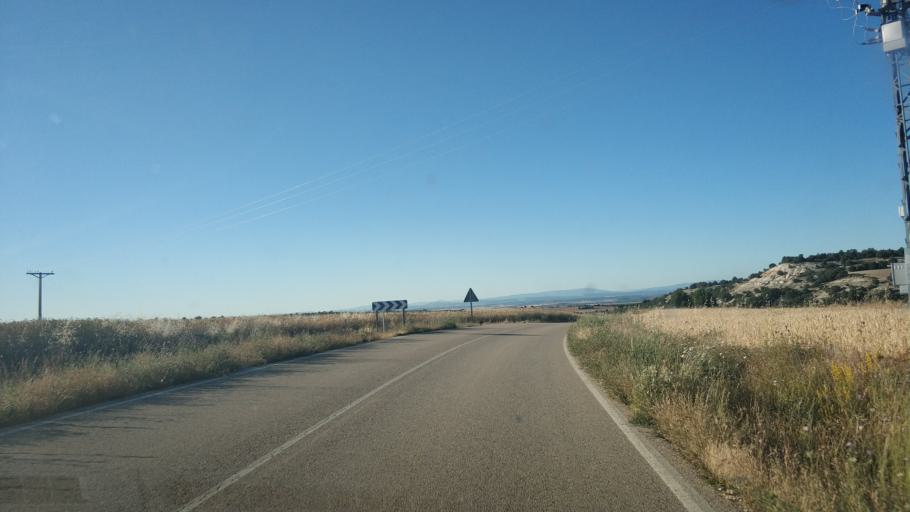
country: ES
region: Castille and Leon
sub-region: Provincia de Soria
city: Liceras
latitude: 41.4683
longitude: -3.2174
